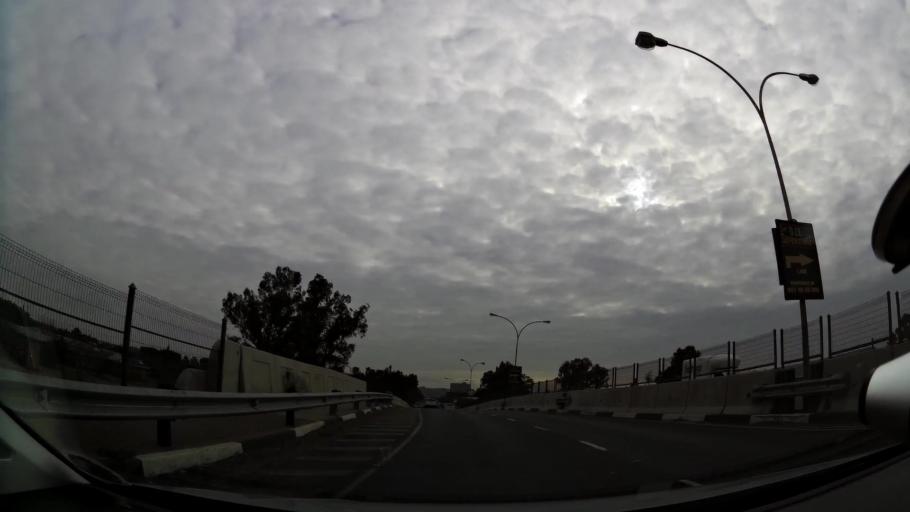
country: ZA
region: Orange Free State
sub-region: Mangaung Metropolitan Municipality
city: Bloemfontein
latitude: -29.1332
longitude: 26.2069
